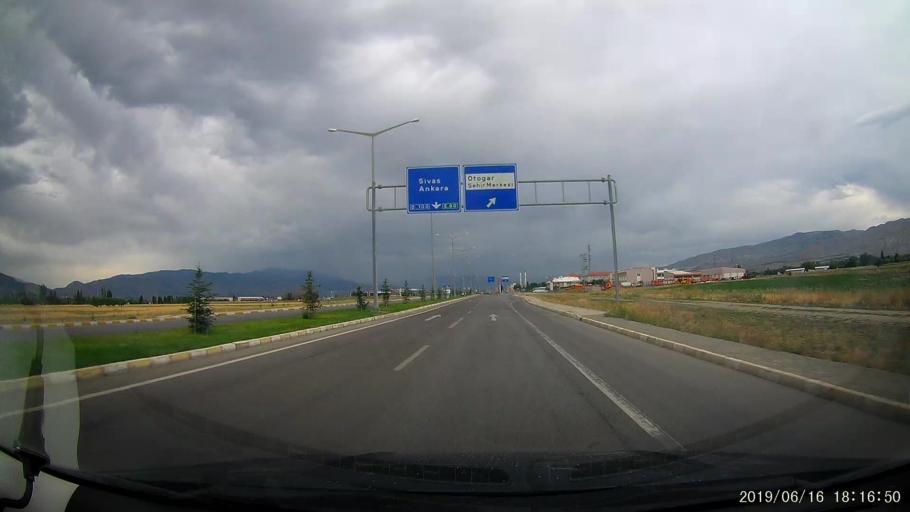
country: TR
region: Erzincan
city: Erzincan
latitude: 39.7308
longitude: 39.5419
